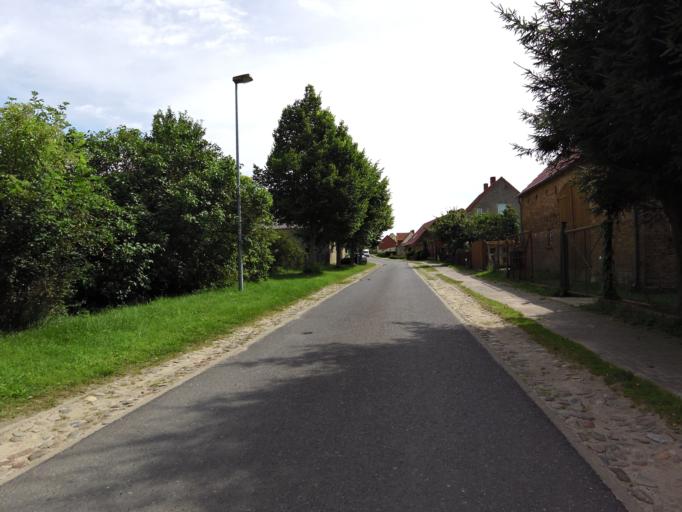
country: DE
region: Brandenburg
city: Lychen
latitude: 53.2902
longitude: 13.3398
